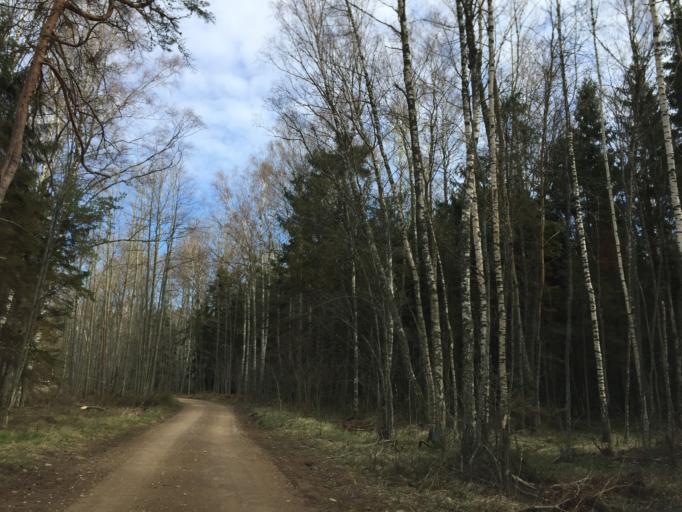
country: LV
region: Salacgrivas
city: Salacgriva
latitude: 57.5848
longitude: 24.3696
